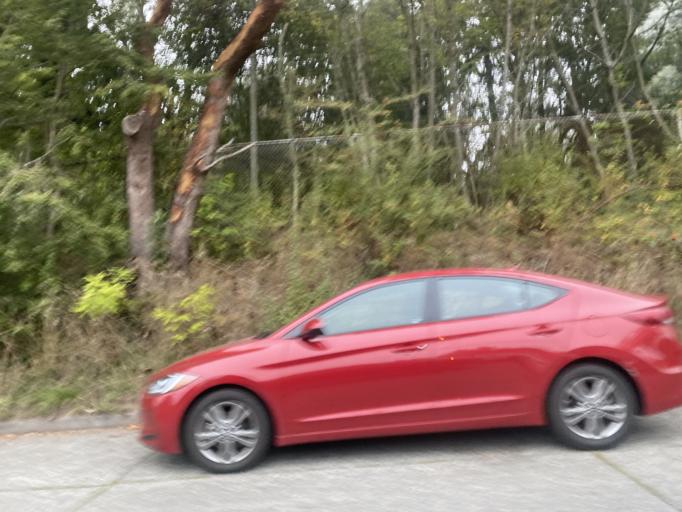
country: US
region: Washington
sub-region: King County
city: Seattle
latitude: 47.6541
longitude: -122.4088
